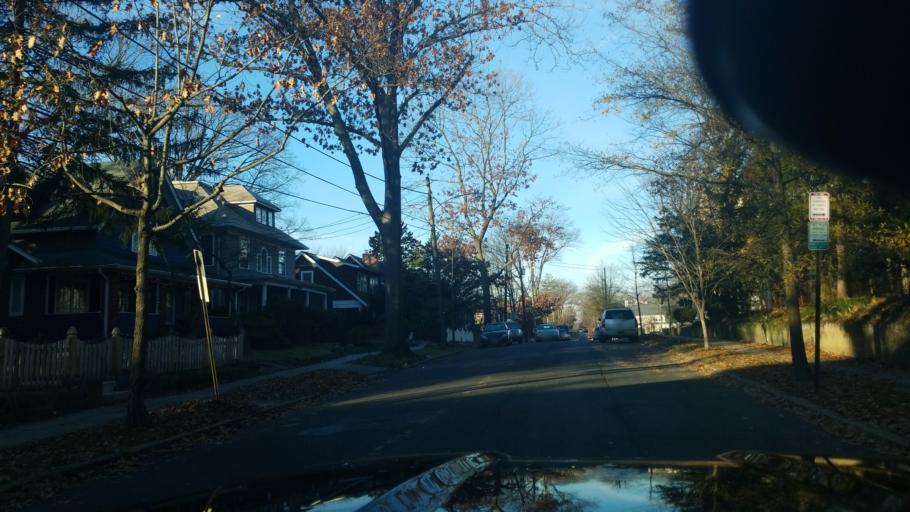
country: US
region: Maryland
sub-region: Montgomery County
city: Takoma Park
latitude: 38.9724
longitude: -77.0214
